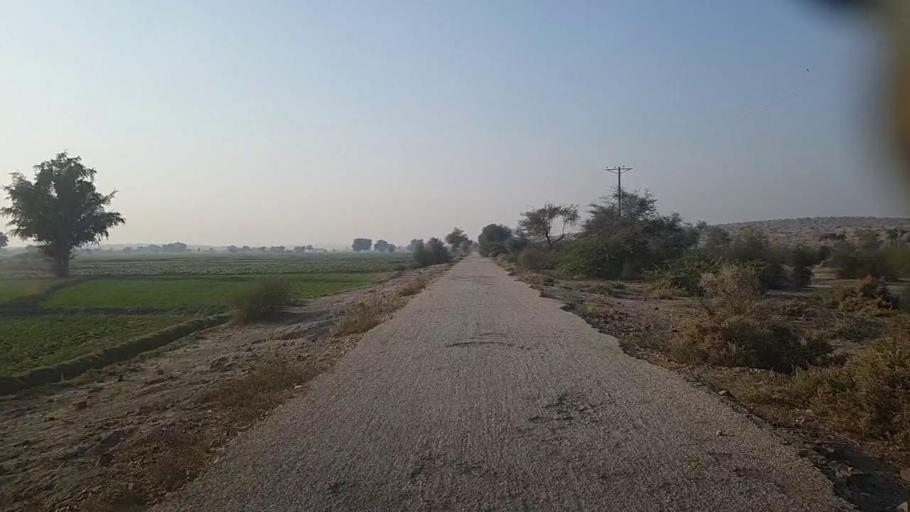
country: PK
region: Sindh
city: Pad Idan
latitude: 26.7167
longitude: 68.4621
